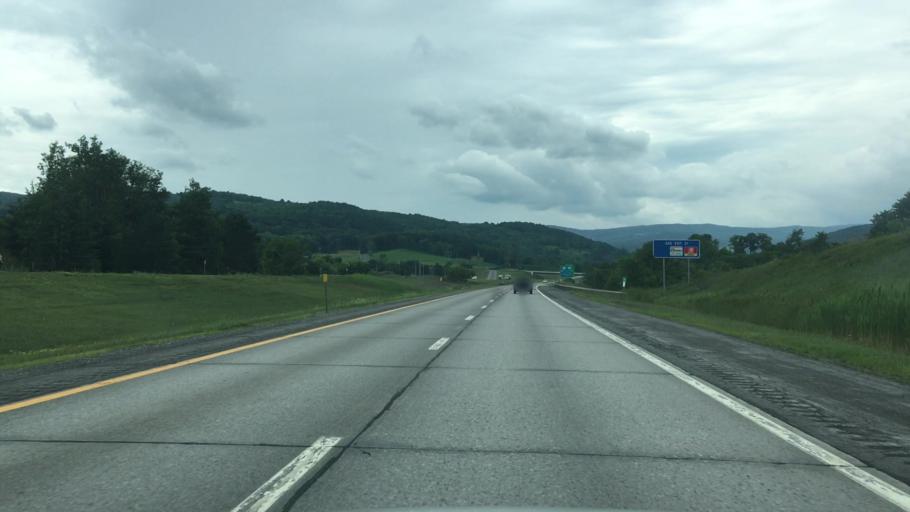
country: US
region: New York
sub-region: Schoharie County
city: Cobleskill
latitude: 42.6598
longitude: -74.5005
